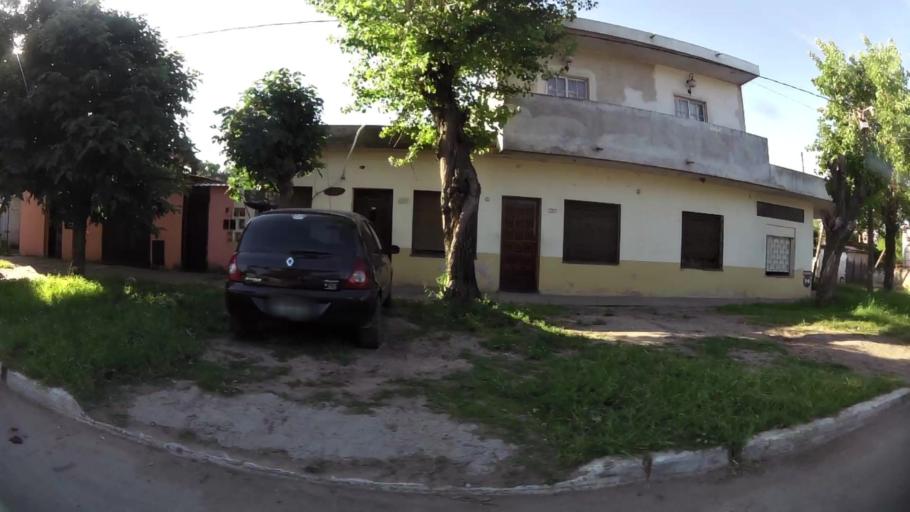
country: AR
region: Buenos Aires
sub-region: Partido de Merlo
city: Merlo
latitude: -34.6841
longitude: -58.7352
